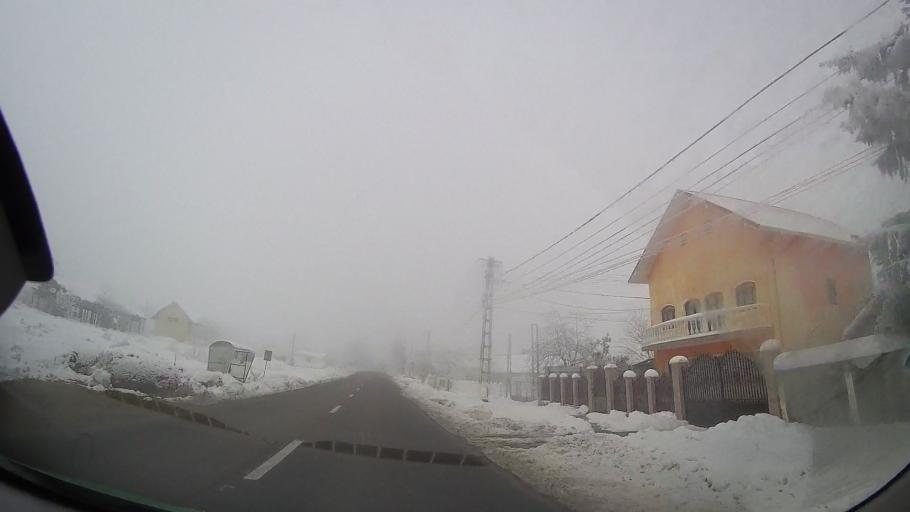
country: RO
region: Iasi
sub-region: Comuna Mircesti
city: Mircesti
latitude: 47.0925
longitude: 26.8210
